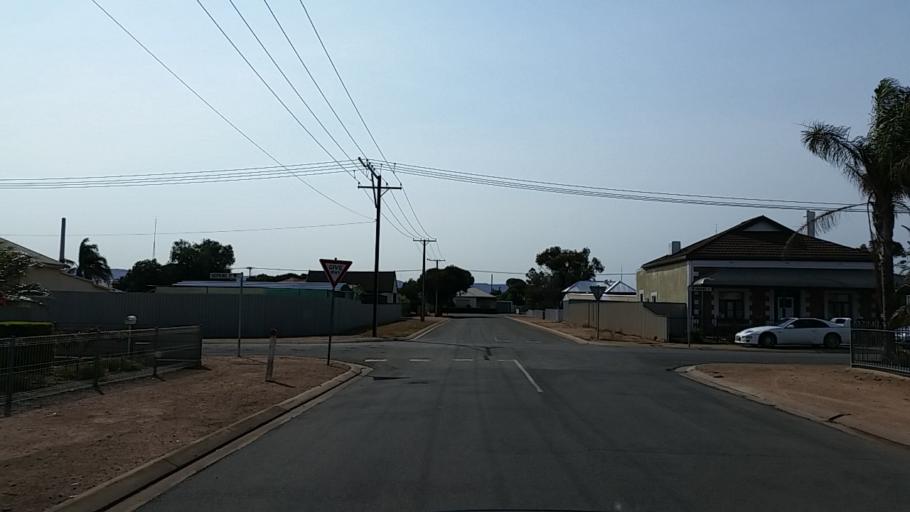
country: AU
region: South Australia
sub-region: Port Pirie City and Dists
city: Port Pirie
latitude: -33.1792
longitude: 137.9920
